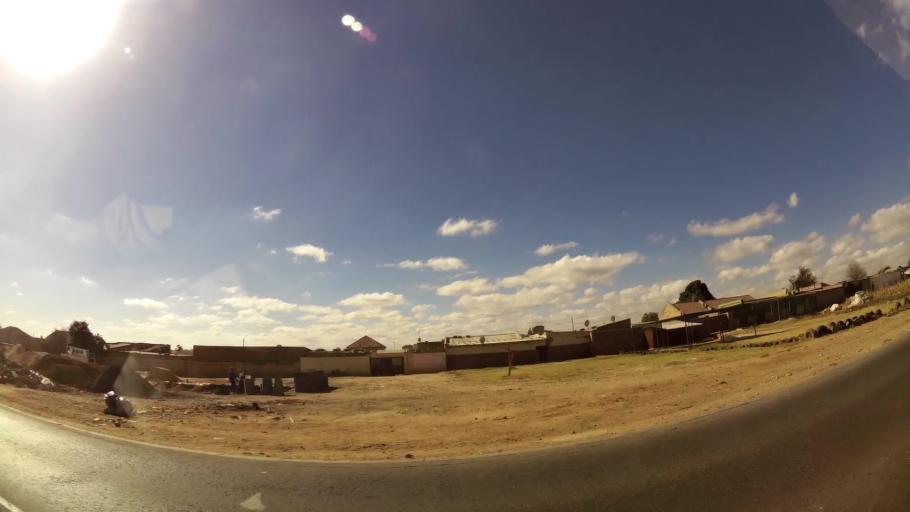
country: ZA
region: Gauteng
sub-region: City of Johannesburg Metropolitan Municipality
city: Modderfontein
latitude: -26.0466
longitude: 28.1753
